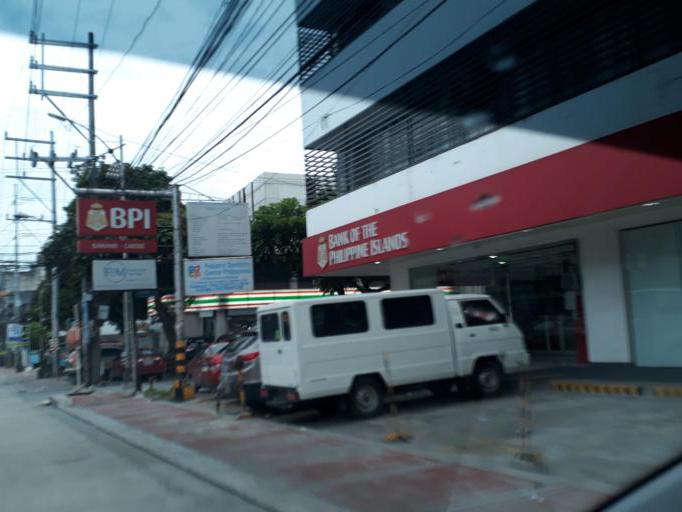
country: PH
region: Calabarzon
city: Del Monte
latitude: 14.6213
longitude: 121.0095
